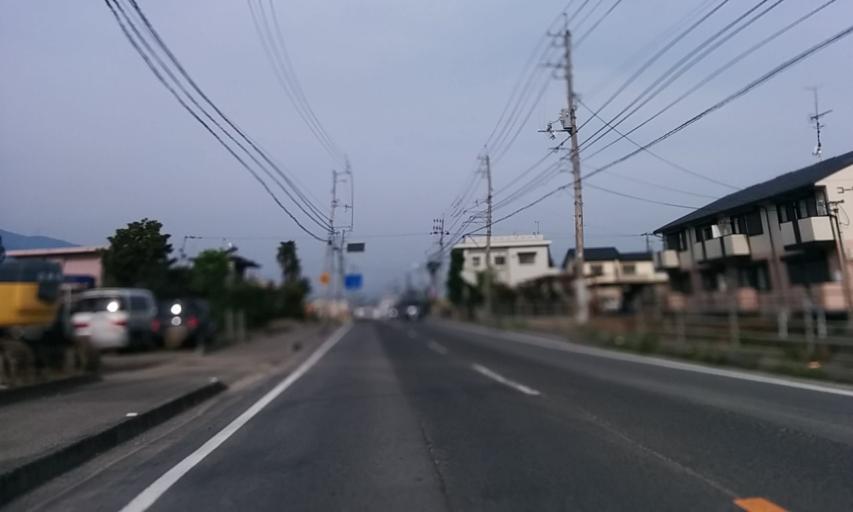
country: JP
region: Ehime
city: Kawanoecho
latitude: 33.9674
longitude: 133.4802
